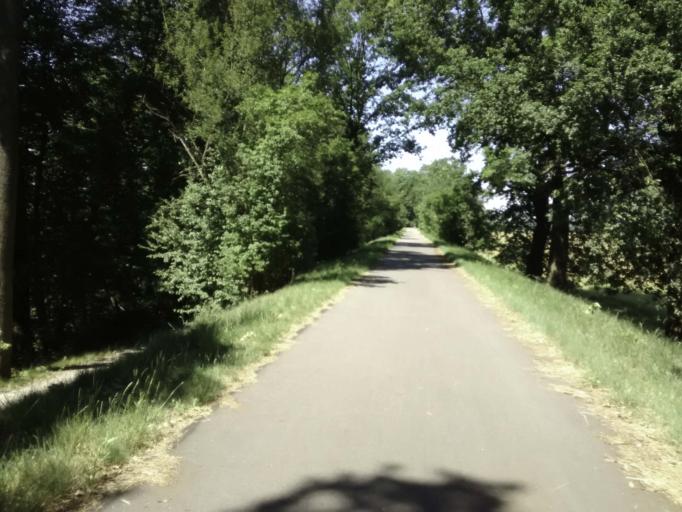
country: DE
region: Saxony-Anhalt
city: Vockerode
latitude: 51.8409
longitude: 12.3788
